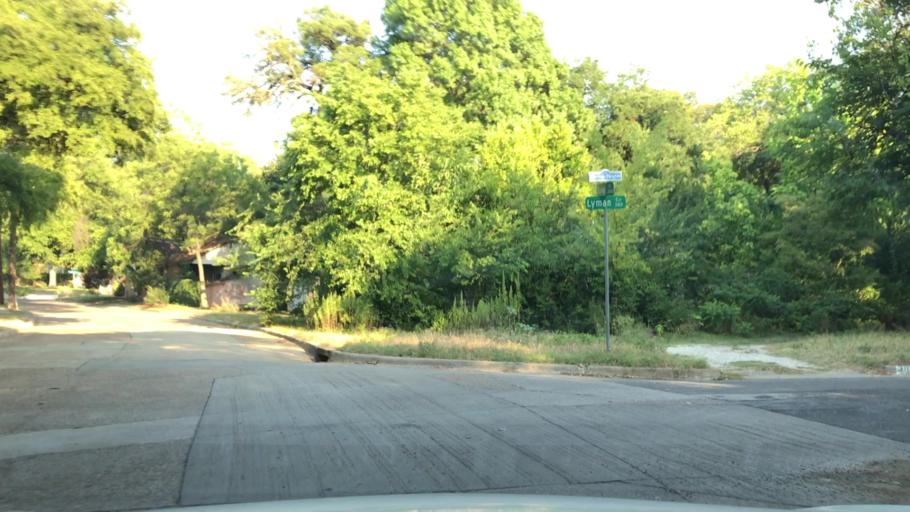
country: US
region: Texas
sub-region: Dallas County
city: Cockrell Hill
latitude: 32.7434
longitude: -96.8666
